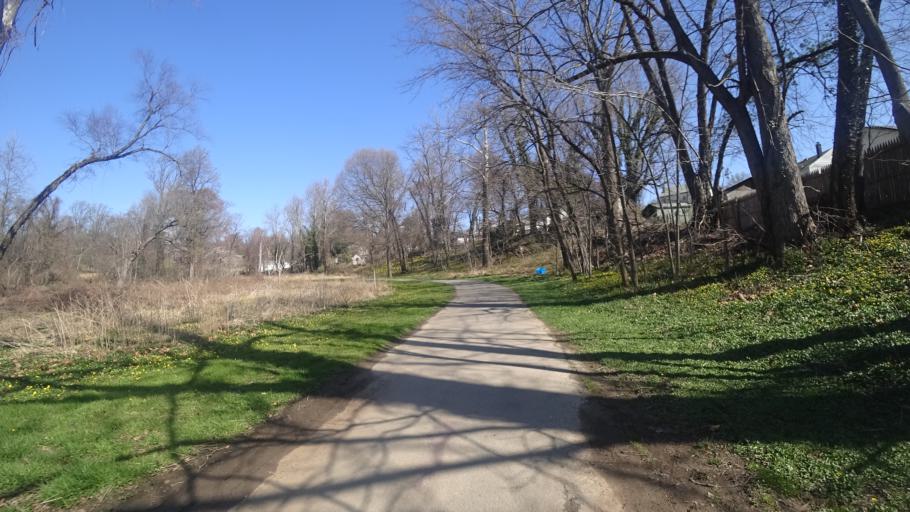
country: US
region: Maryland
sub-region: Prince George's County
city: Chillum
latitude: 38.9743
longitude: -76.9823
